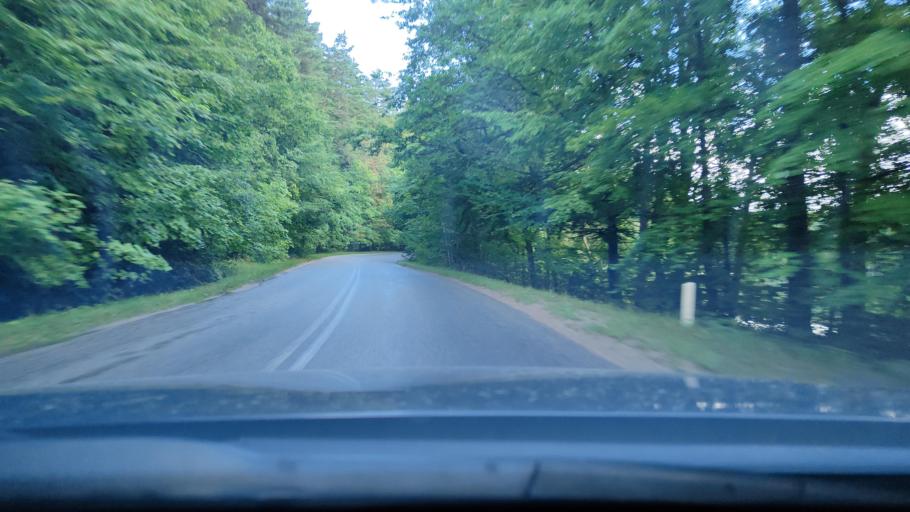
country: PL
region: Pomeranian Voivodeship
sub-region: Powiat pucki
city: Krokowa
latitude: 54.7141
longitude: 18.1654
